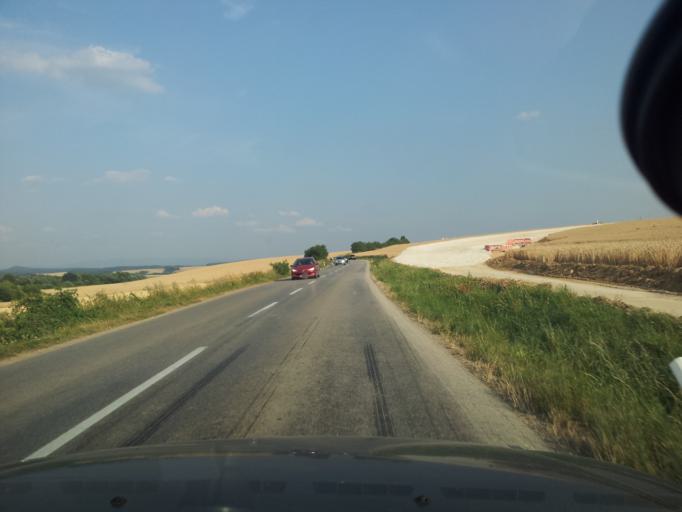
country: SK
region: Nitriansky
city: Banovce nad Bebravou
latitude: 48.7466
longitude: 18.2242
